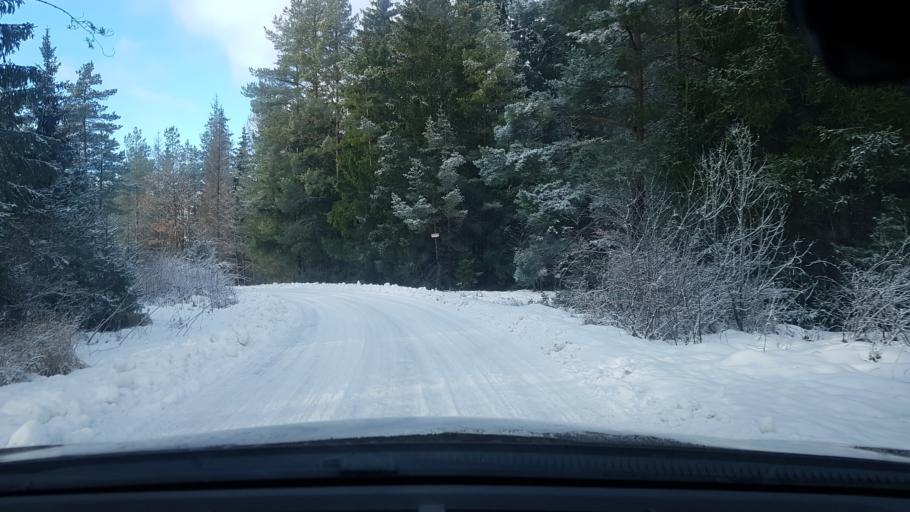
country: EE
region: Harju
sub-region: Keila linn
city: Keila
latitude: 59.2818
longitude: 24.2627
